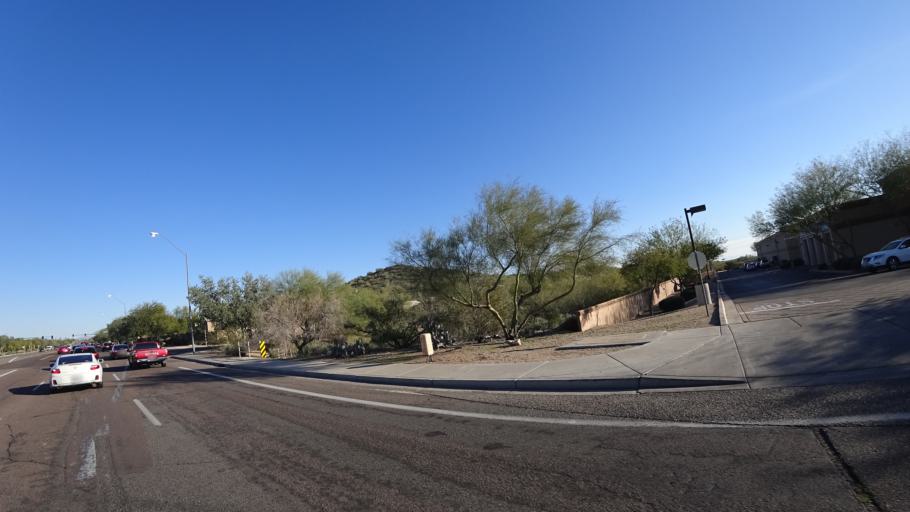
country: US
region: Arizona
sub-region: Maricopa County
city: Sun City
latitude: 33.7121
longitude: -112.1999
